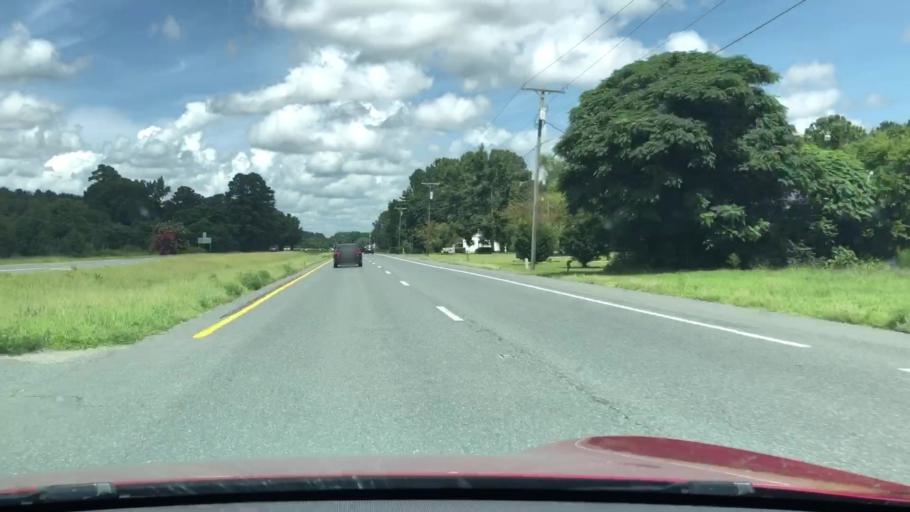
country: US
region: Virginia
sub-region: Northampton County
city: Eastville
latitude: 37.3887
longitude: -75.9158
